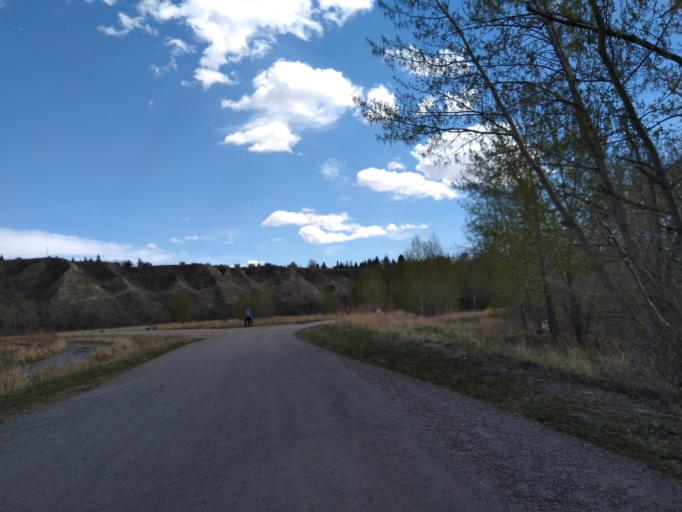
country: CA
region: Alberta
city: Calgary
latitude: 51.0872
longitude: -114.1731
